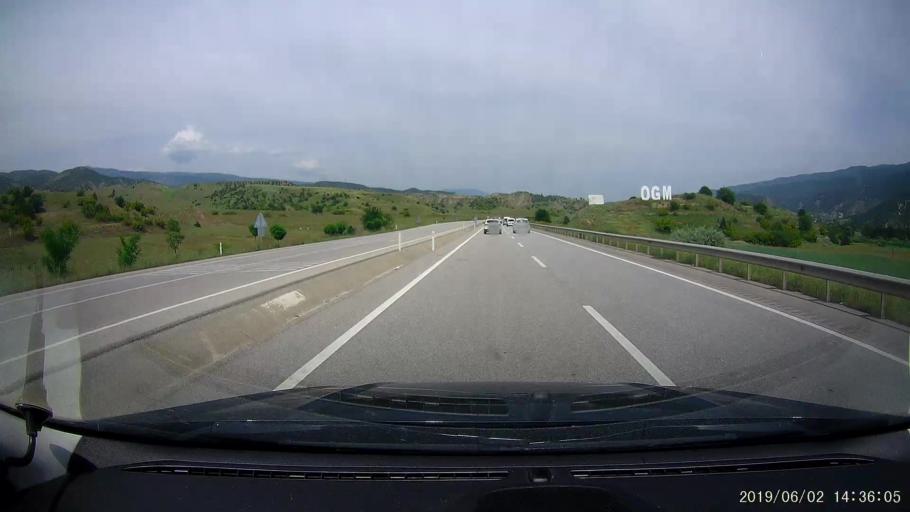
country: TR
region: Kastamonu
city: Tosya
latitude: 41.0444
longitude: 34.2279
